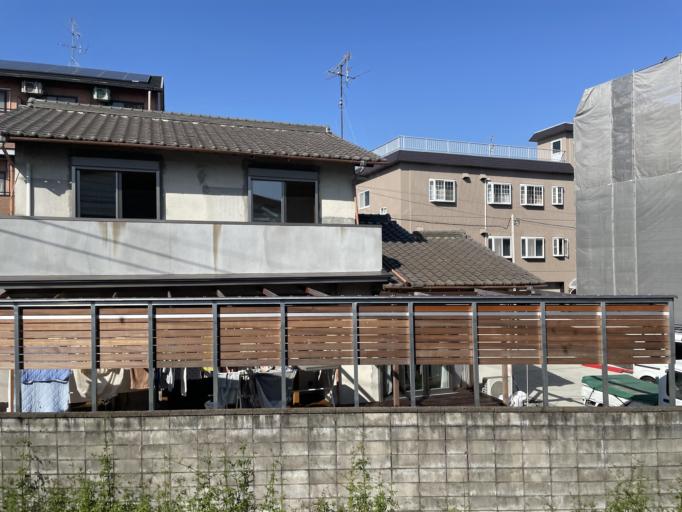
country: JP
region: Nara
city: Nara-shi
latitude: 34.6974
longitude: 135.7759
